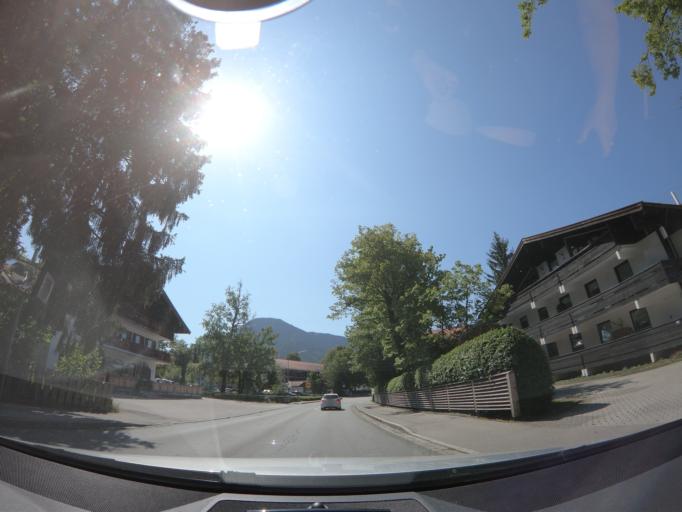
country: DE
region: Bavaria
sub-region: Upper Bavaria
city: Rottach-Egern
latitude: 47.6964
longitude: 11.7731
